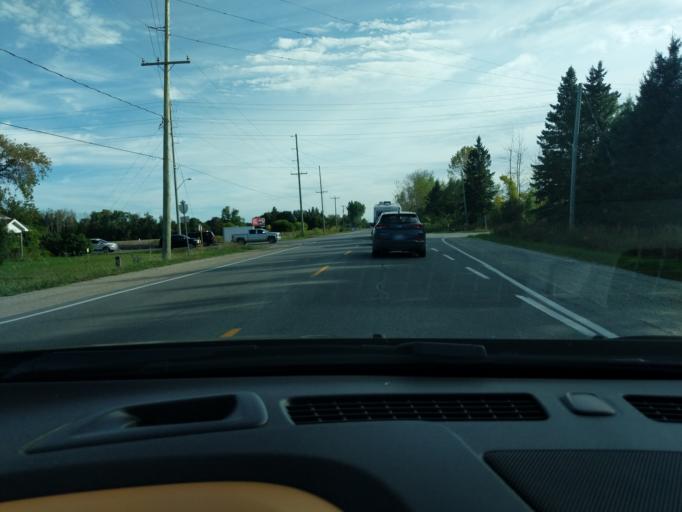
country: CA
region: Ontario
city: Wasaga Beach
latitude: 44.4353
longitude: -80.0999
